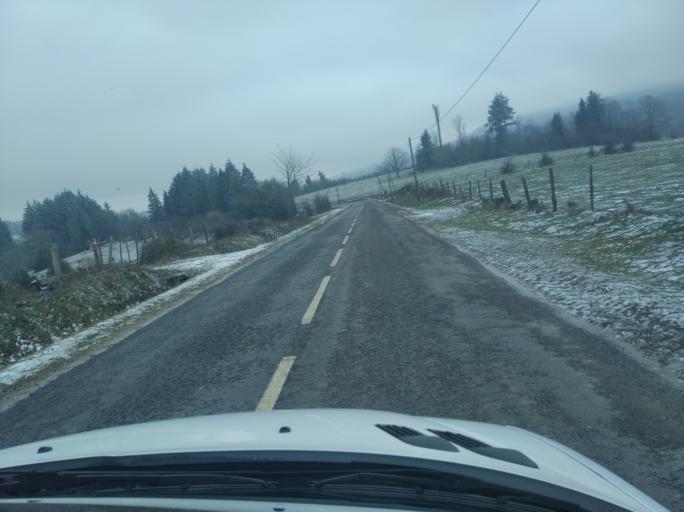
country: FR
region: Rhone-Alpes
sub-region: Departement de la Loire
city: La Pacaudiere
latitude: 46.1197
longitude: 3.7900
